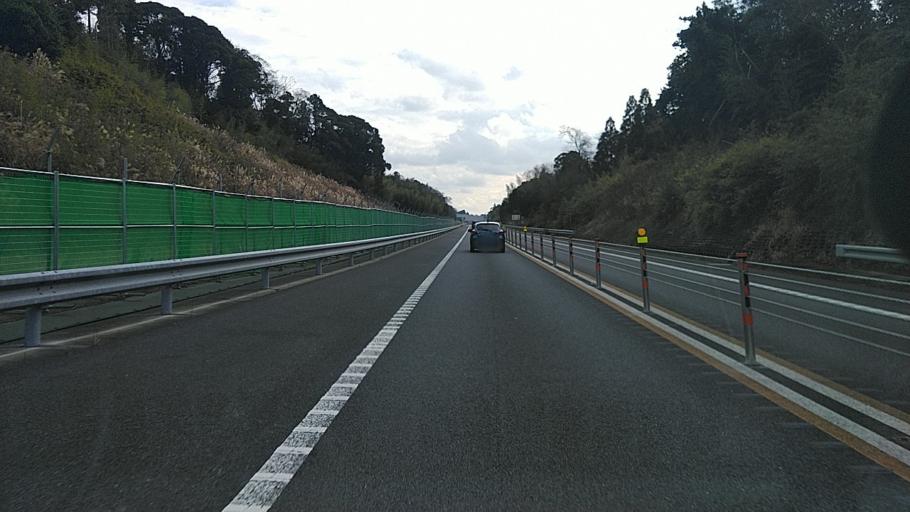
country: JP
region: Ibaraki
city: Edosaki
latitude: 35.8780
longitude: 140.3862
